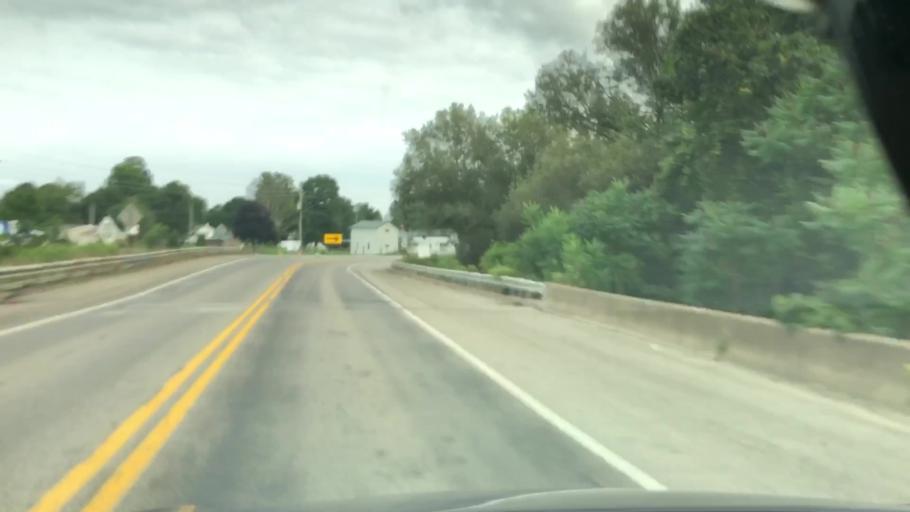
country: US
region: Pennsylvania
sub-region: Erie County
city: Union City
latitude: 42.0059
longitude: -79.8121
